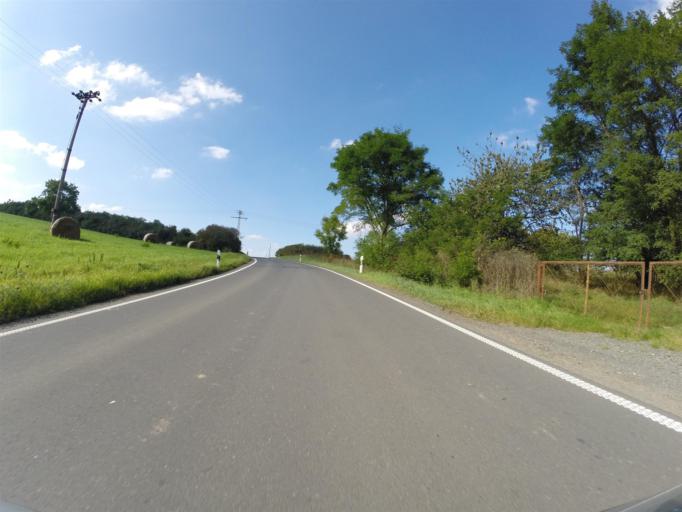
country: DE
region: Thuringia
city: Schongleina
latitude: 50.9295
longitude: 11.7214
